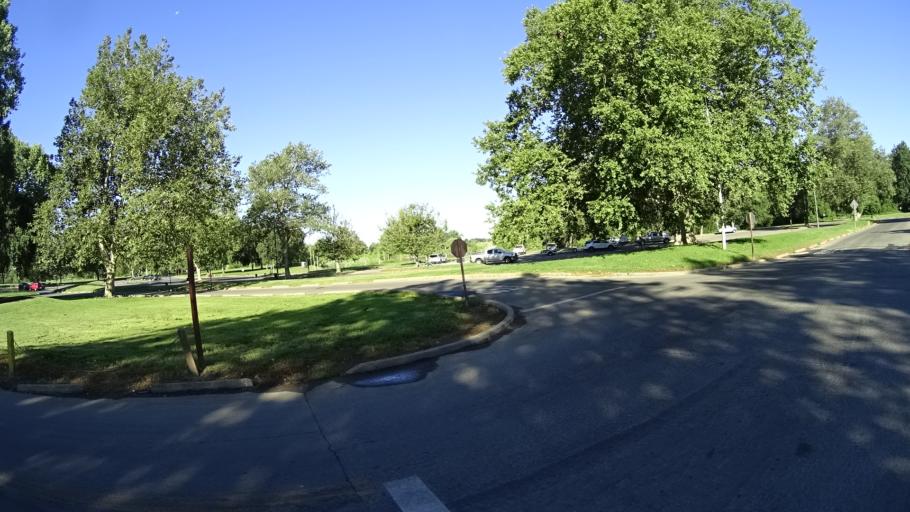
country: US
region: California
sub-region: Sacramento County
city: Sacramento
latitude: 38.6012
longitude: -121.5078
